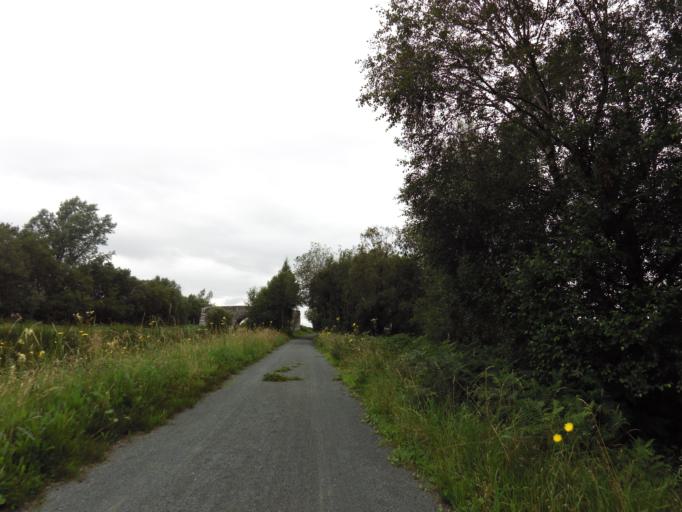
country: IE
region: Leinster
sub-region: An Iarmhi
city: Moate
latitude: 53.5859
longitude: -7.6235
